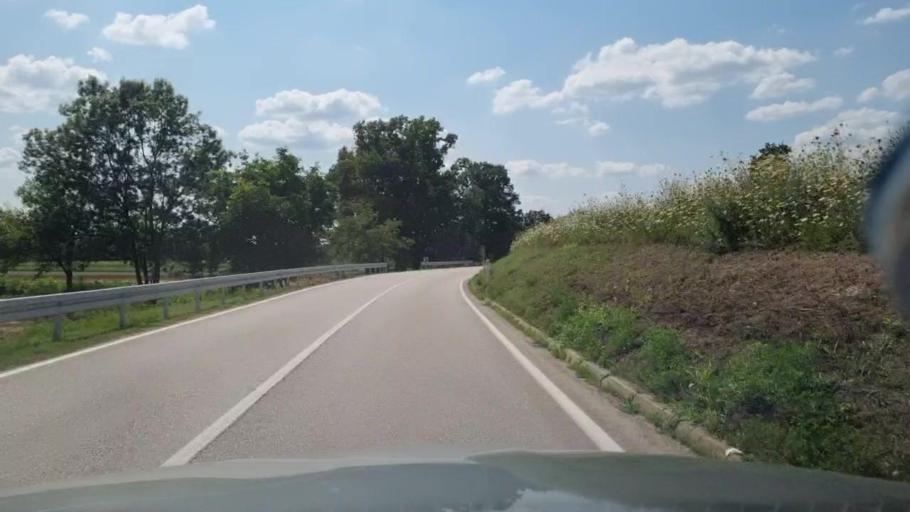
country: BA
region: Federation of Bosnia and Herzegovina
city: Donja Mahala
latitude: 45.0549
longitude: 18.6381
